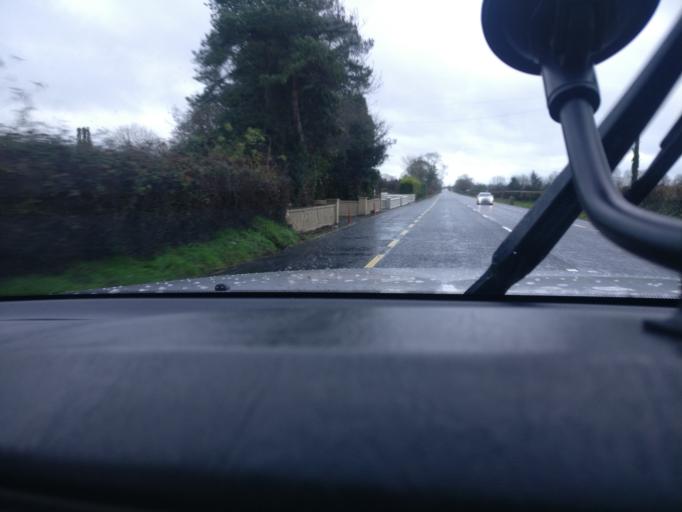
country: IE
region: Leinster
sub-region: An Mhi
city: Enfield
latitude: 53.4210
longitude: -6.8562
